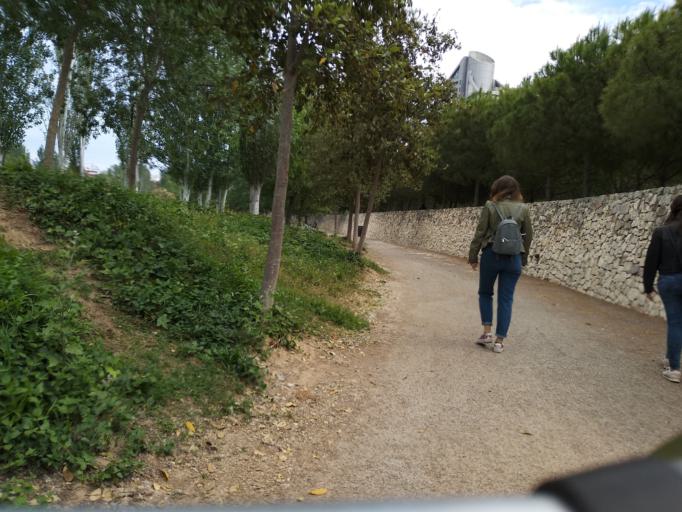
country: ES
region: Valencia
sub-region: Provincia de Valencia
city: Mislata
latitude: 39.4749
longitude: -0.4098
